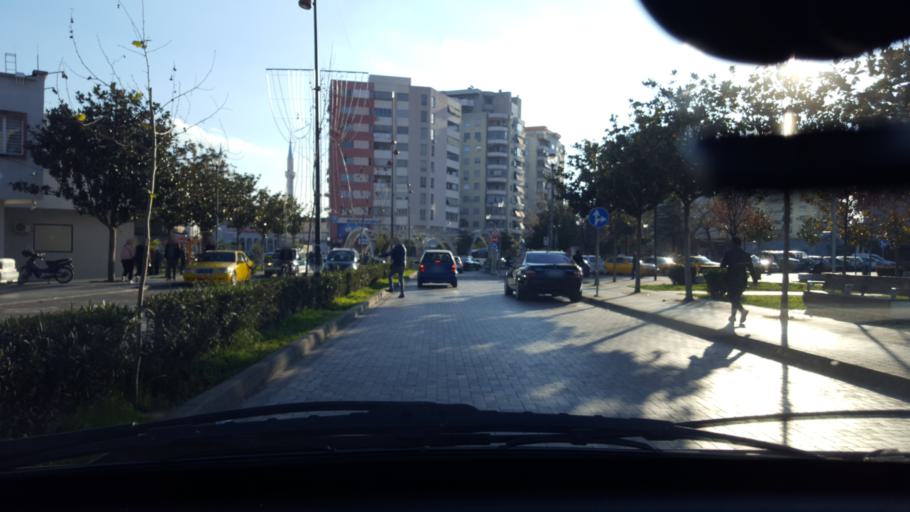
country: AL
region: Elbasan
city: Elbasan
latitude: 41.1115
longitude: 20.0796
